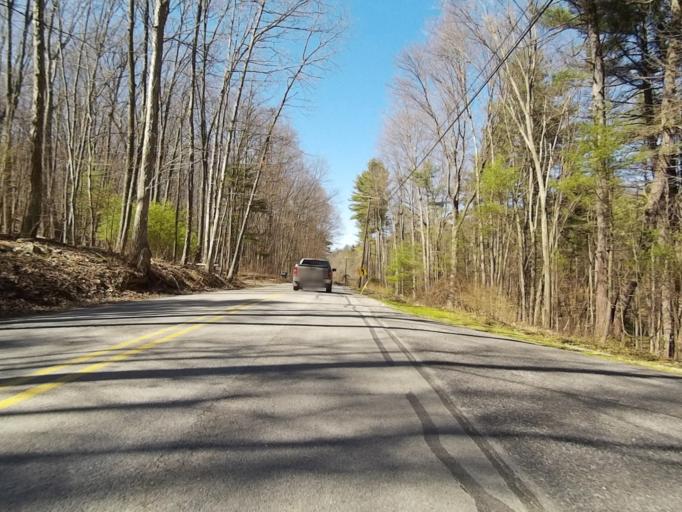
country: US
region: Pennsylvania
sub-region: Centre County
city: Stormstown
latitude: 40.7483
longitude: -78.0313
